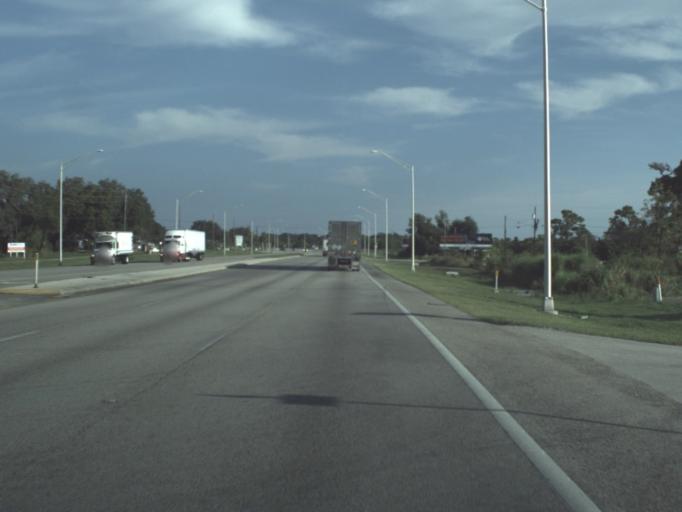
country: US
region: Florida
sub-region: Highlands County
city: Avon Park
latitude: 27.6246
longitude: -81.5146
